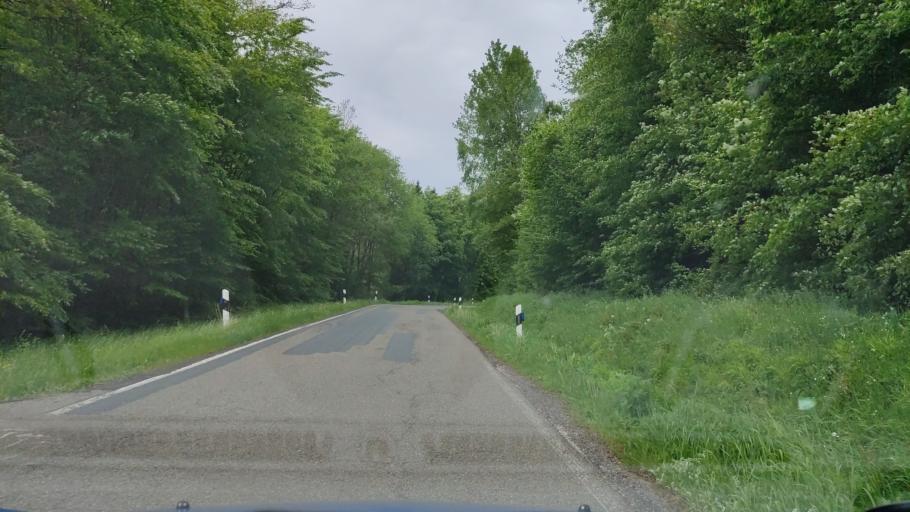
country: DE
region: Lower Saxony
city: Dassel
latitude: 51.7061
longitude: 9.7342
